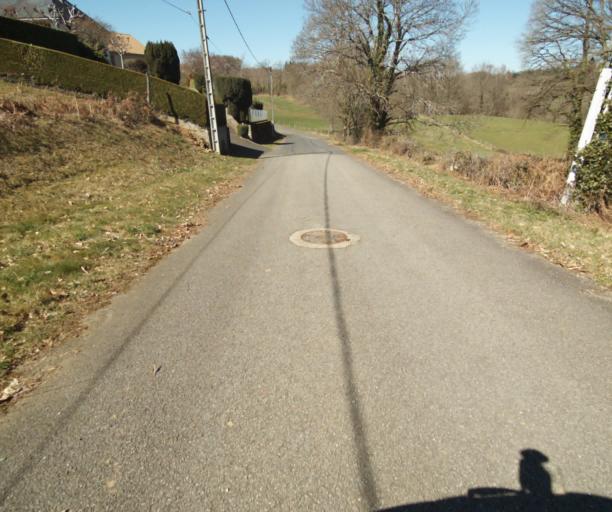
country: FR
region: Limousin
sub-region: Departement de la Correze
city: Seilhac
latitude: 45.3733
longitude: 1.6884
